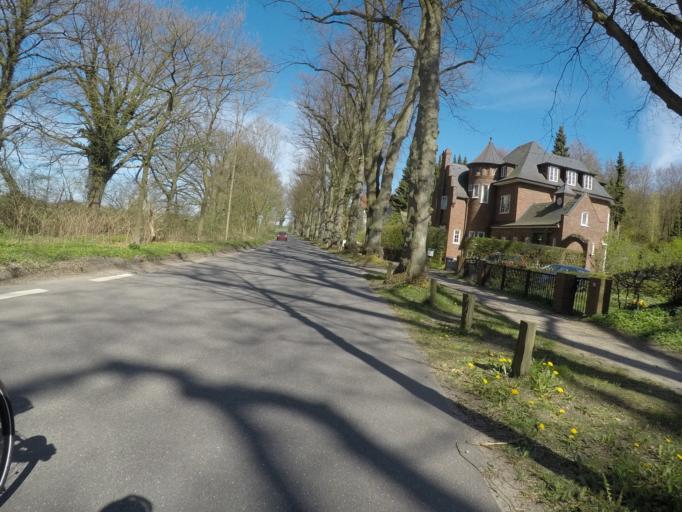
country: DE
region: Hamburg
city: Wohldorf-Ohlstedt
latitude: 53.7075
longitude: 10.1229
